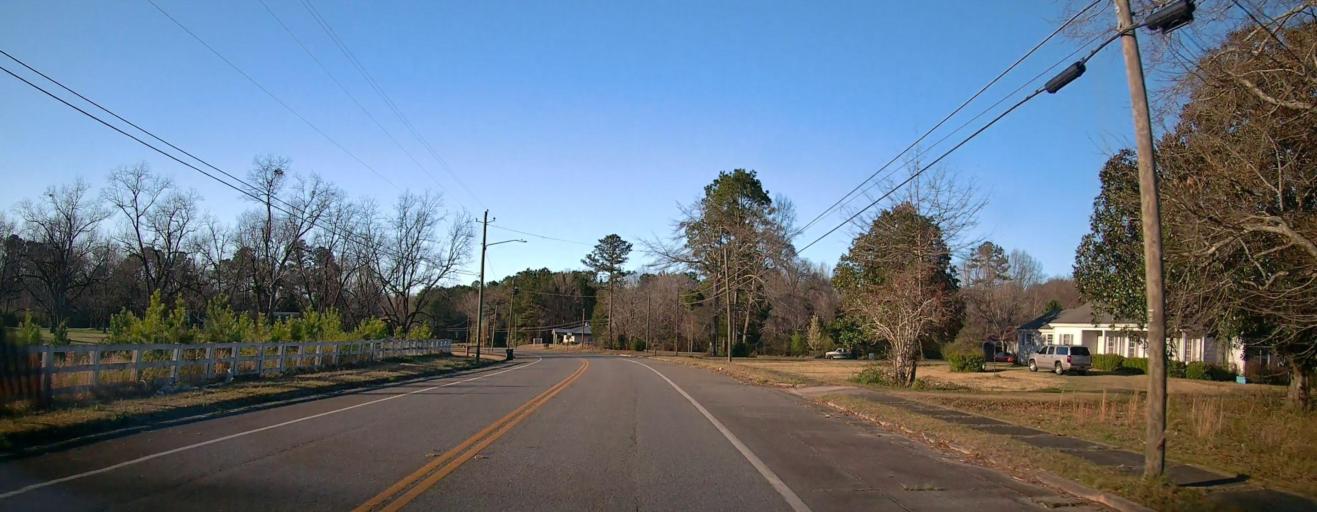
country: US
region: Georgia
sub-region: Talbot County
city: Talbotton
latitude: 32.6670
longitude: -84.5339
